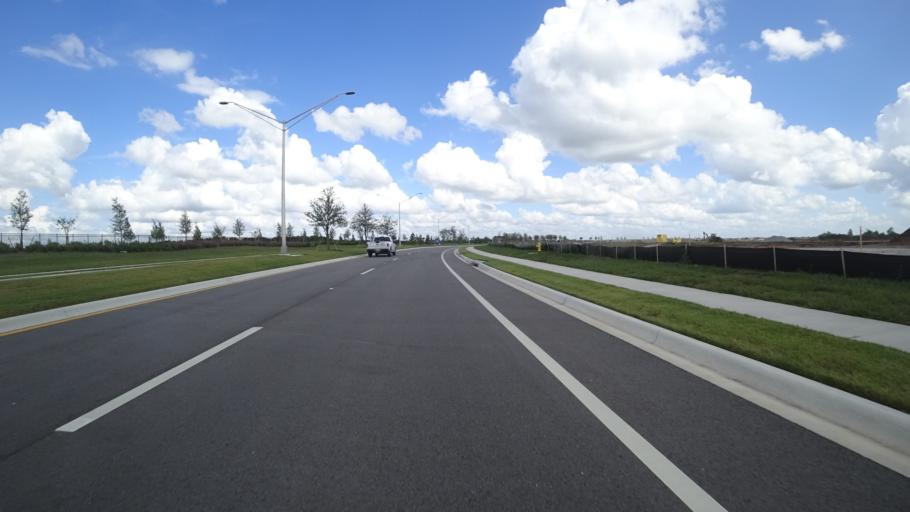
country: US
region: Florida
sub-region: Sarasota County
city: The Meadows
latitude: 27.4490
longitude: -82.3657
